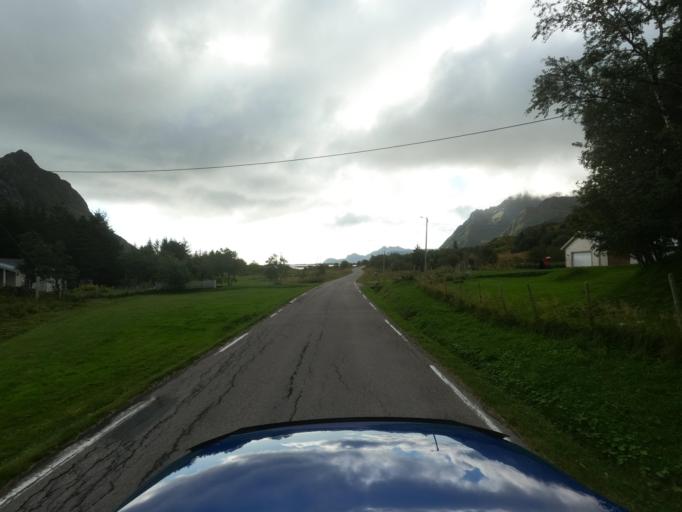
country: NO
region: Nordland
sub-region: Vestvagoy
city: Evjen
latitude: 68.1992
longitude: 13.8857
